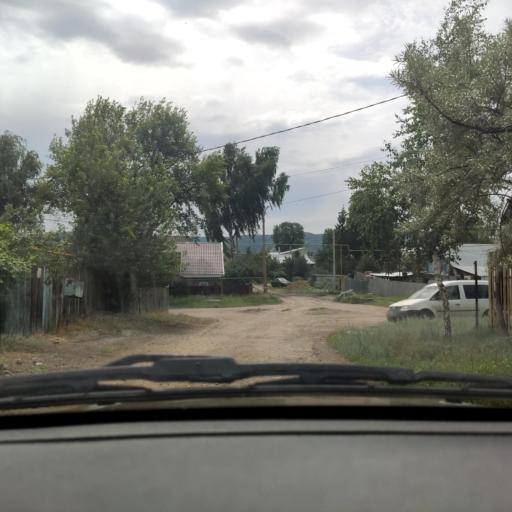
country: RU
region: Samara
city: Zhigulevsk
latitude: 53.4708
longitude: 49.6179
